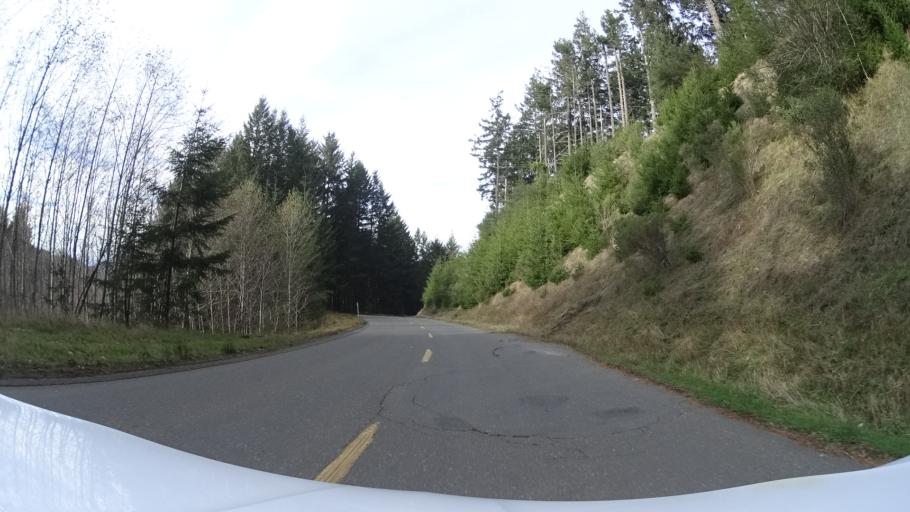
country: US
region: California
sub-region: Humboldt County
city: Ferndale
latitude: 40.5214
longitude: -124.2667
